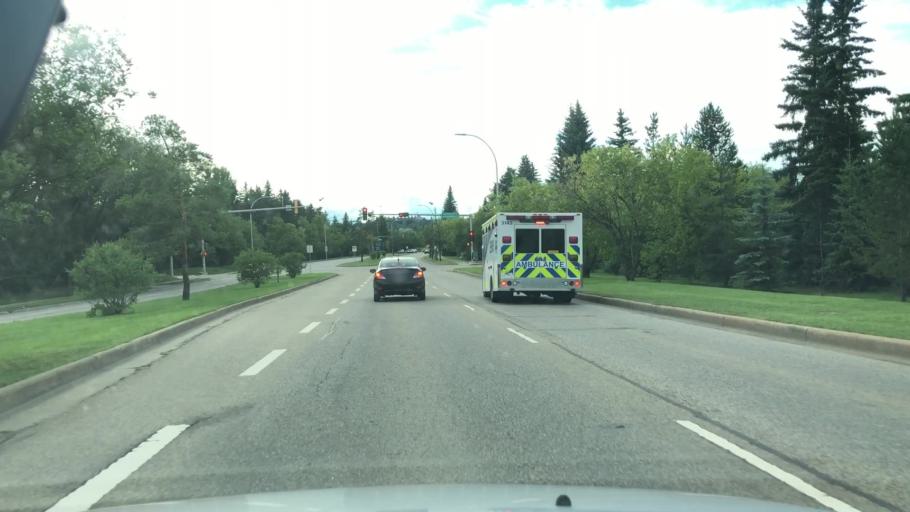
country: CA
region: Alberta
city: St. Albert
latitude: 53.6437
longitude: -113.6070
